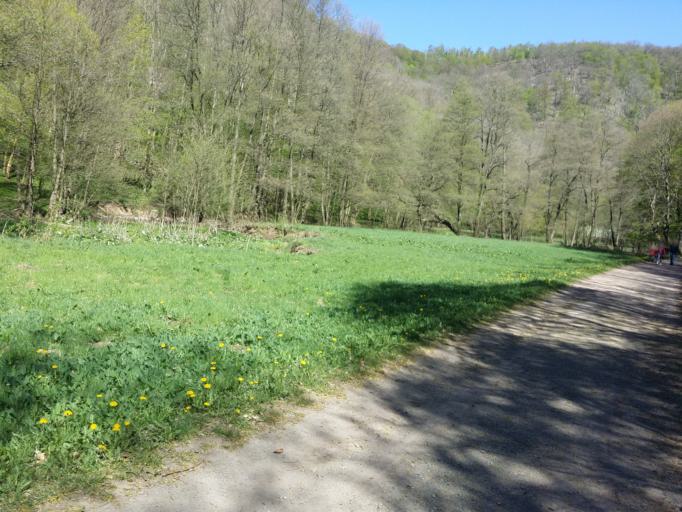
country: DE
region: Saxony-Anhalt
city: Ballenstedt
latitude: 51.6845
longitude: 11.2573
